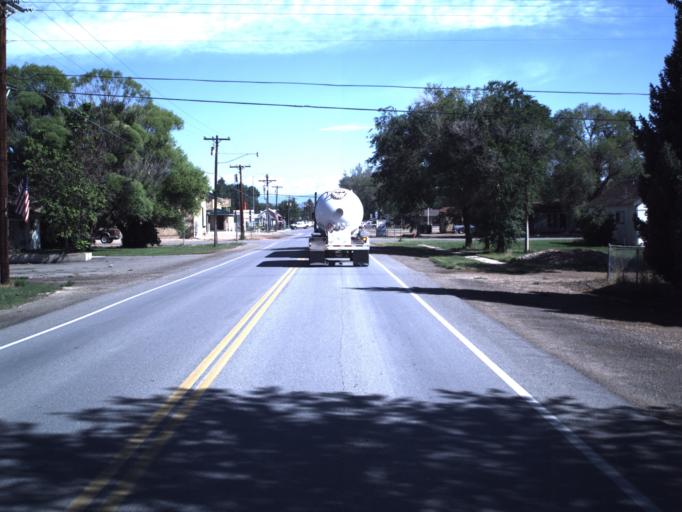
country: US
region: Utah
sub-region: Duchesne County
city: Duchesne
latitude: 40.1614
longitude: -110.4031
